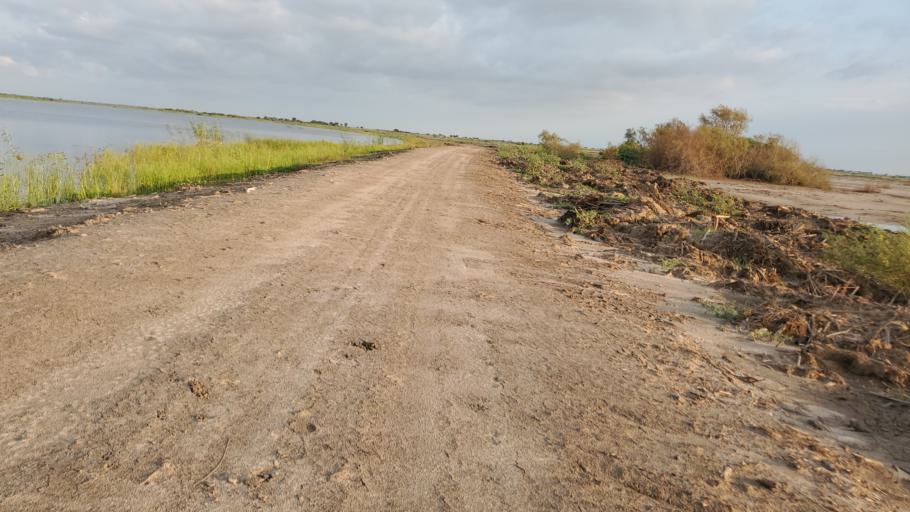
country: SN
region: Saint-Louis
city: Saint-Louis
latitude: 16.0245
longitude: -16.4099
